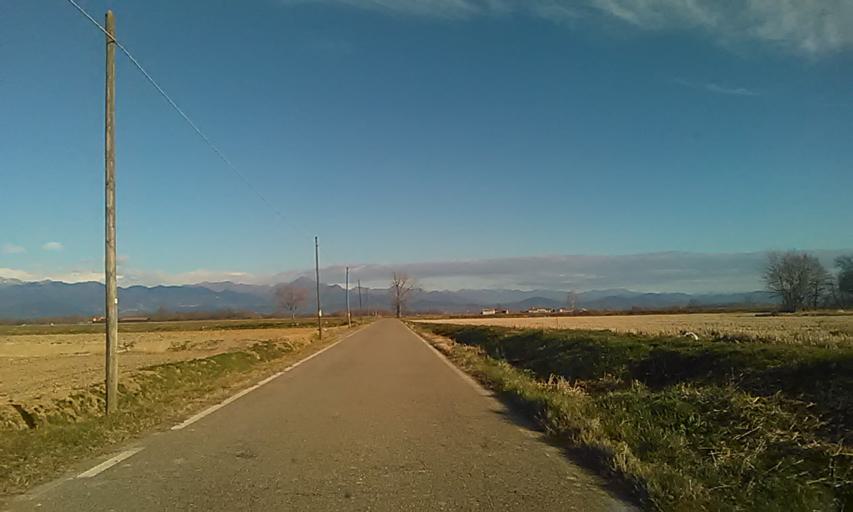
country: IT
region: Piedmont
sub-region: Provincia di Vercelli
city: Buronzo
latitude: 45.4942
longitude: 8.2706
